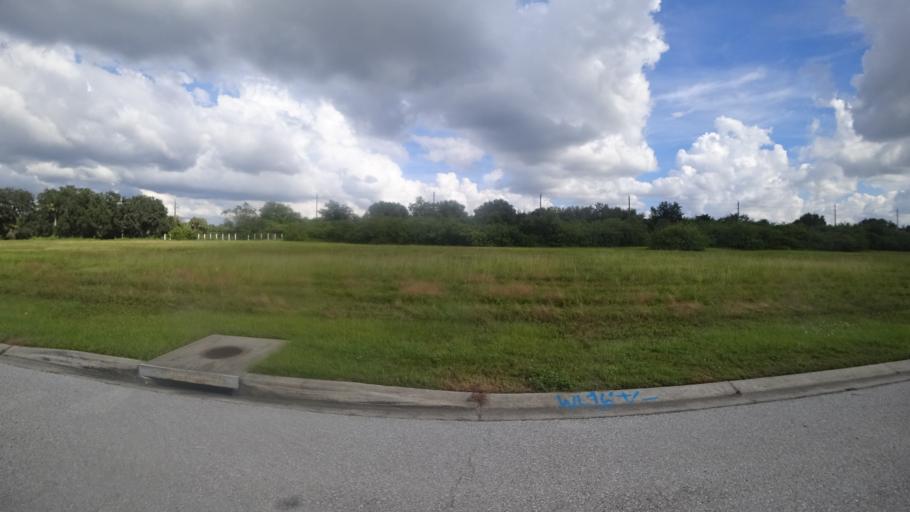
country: US
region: Florida
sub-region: Manatee County
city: Memphis
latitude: 27.6194
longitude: -82.5285
